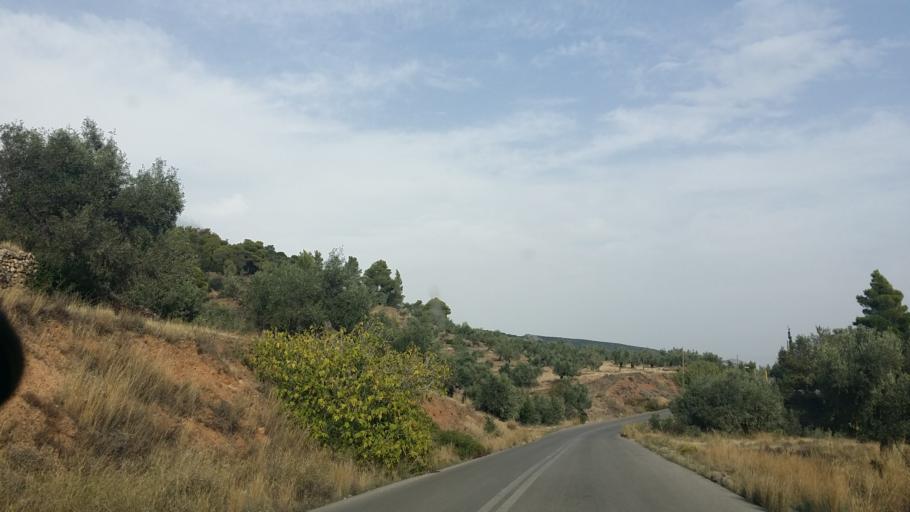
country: GR
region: Central Greece
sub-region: Nomos Voiotias
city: Korini
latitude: 38.2590
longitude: 22.8991
